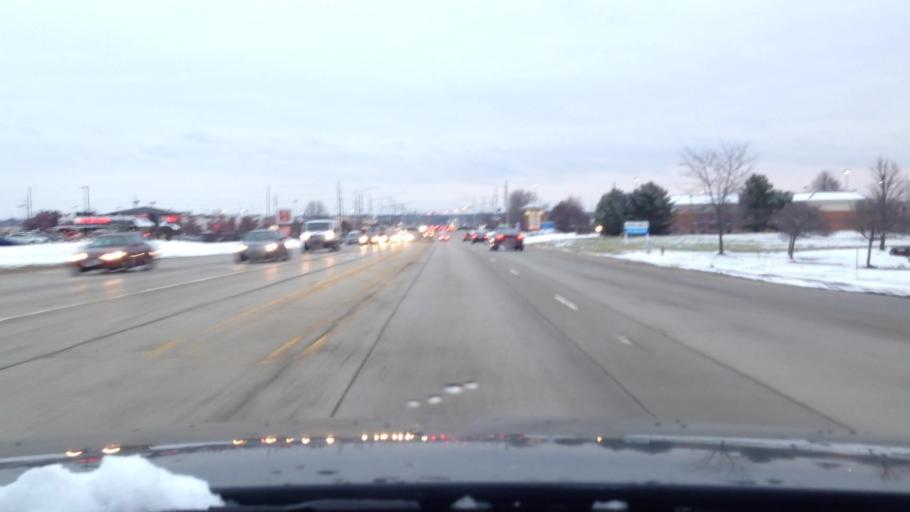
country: US
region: Illinois
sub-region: McHenry County
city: Lake in the Hills
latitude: 42.1721
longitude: -88.3353
